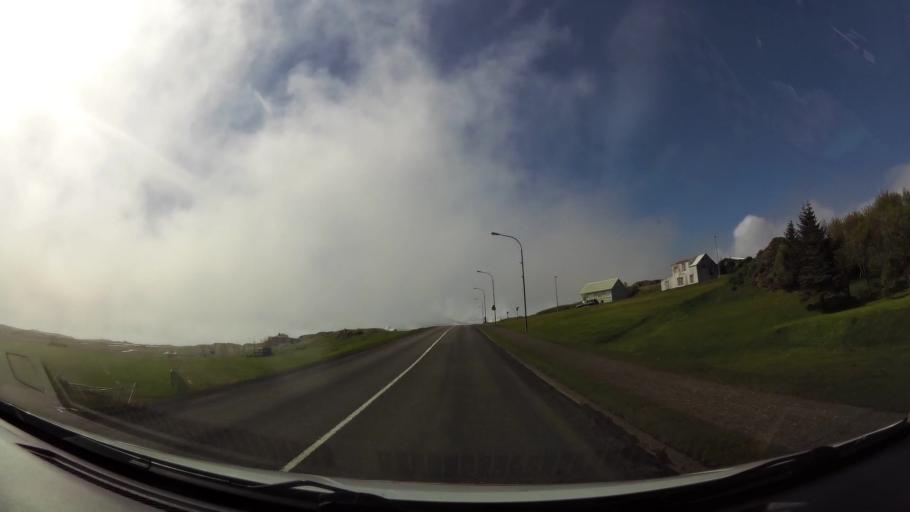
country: IS
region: East
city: Reydarfjoerdur
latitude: 64.6544
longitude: -14.2933
